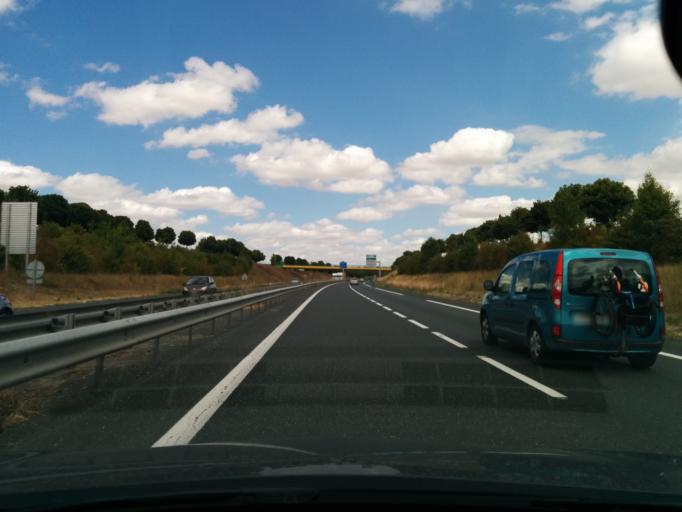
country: FR
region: Centre
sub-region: Departement de l'Indre
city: Saint-Maur
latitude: 46.8201
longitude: 1.6266
